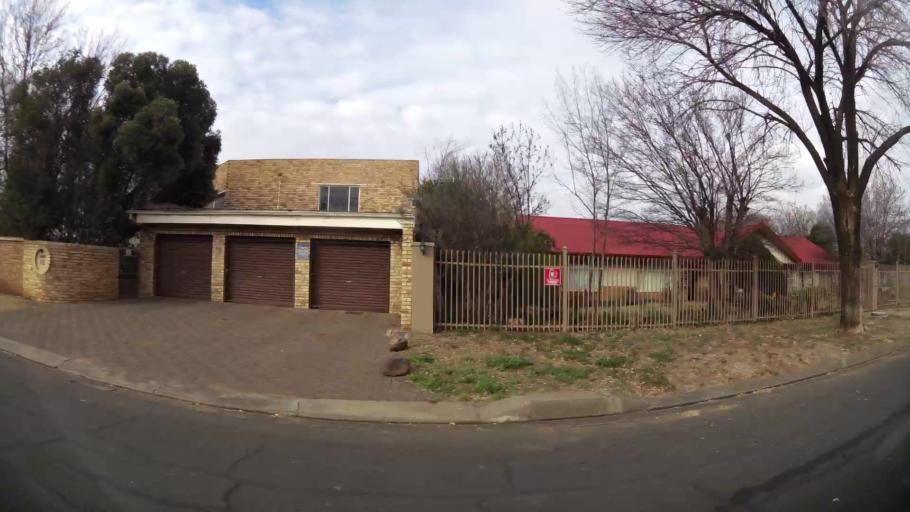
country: ZA
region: Orange Free State
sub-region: Mangaung Metropolitan Municipality
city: Bloemfontein
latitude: -29.1204
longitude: 26.1814
